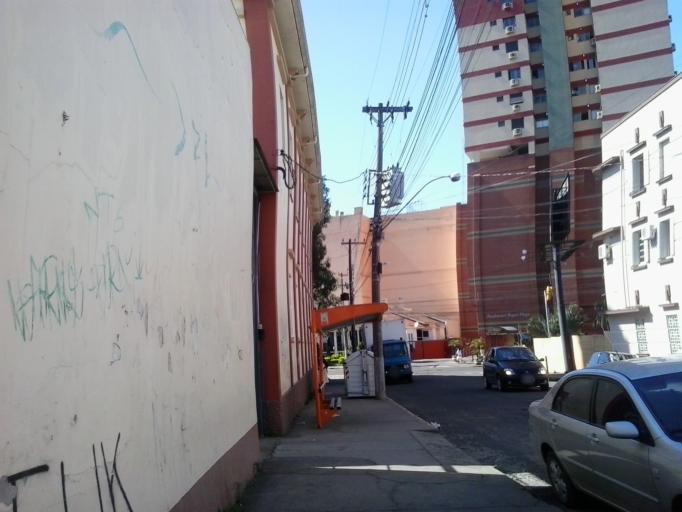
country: BR
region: Rio Grande do Sul
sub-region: Santa Maria
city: Santa Maria
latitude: -29.6890
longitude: -53.7952
